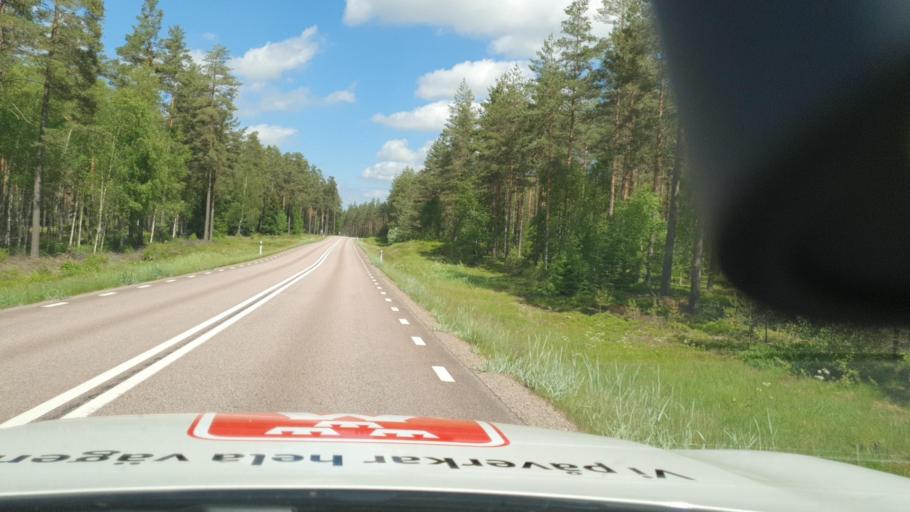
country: SE
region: Vaermland
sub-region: Filipstads Kommun
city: Filipstad
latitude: 59.6328
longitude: 13.9544
